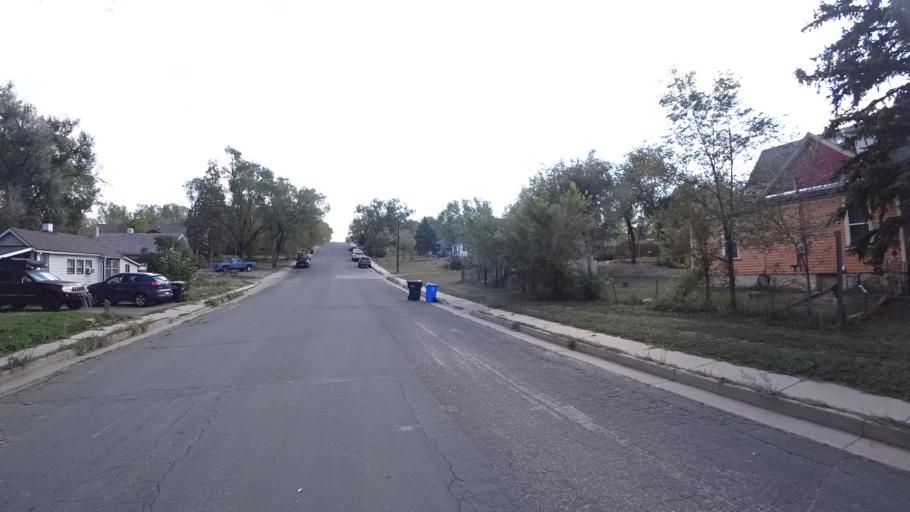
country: US
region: Colorado
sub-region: El Paso County
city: Colorado Springs
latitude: 38.8293
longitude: -104.8130
